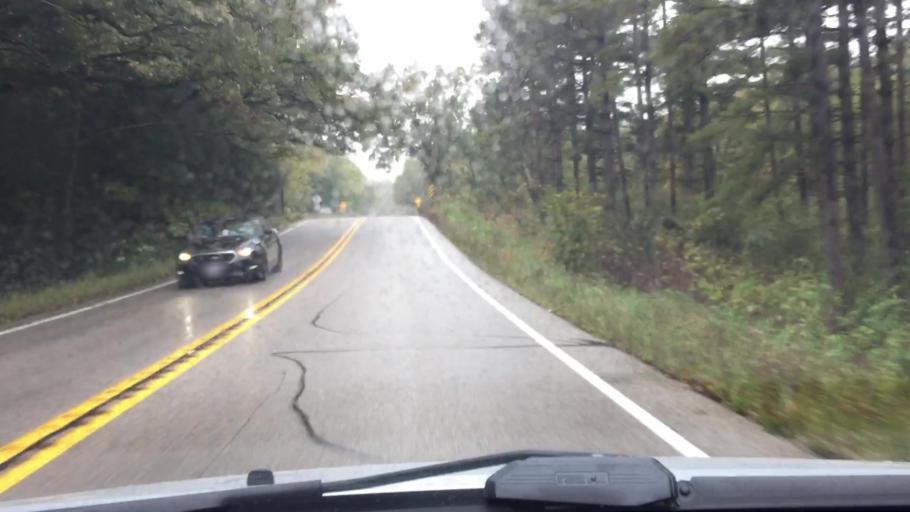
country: US
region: Wisconsin
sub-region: Waukesha County
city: Eagle
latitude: 42.9215
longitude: -88.4705
